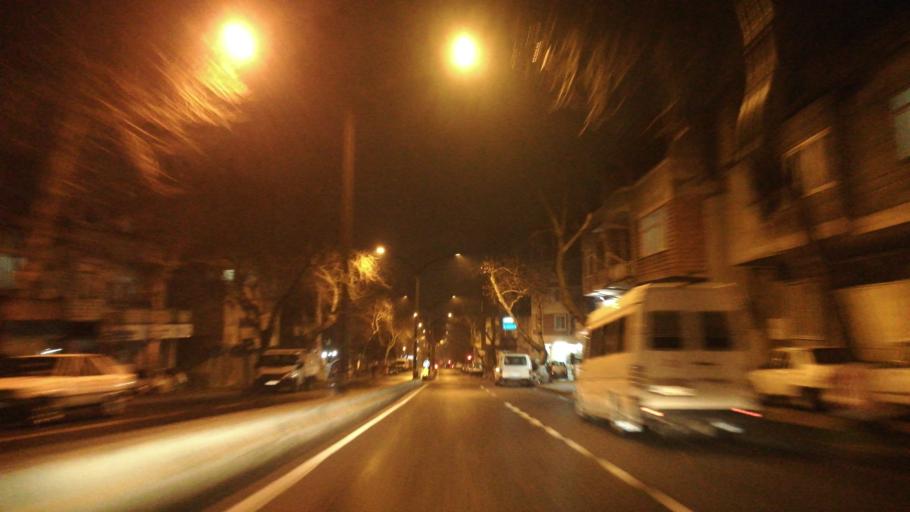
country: TR
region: Kahramanmaras
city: Kahramanmaras
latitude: 37.5769
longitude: 36.9192
